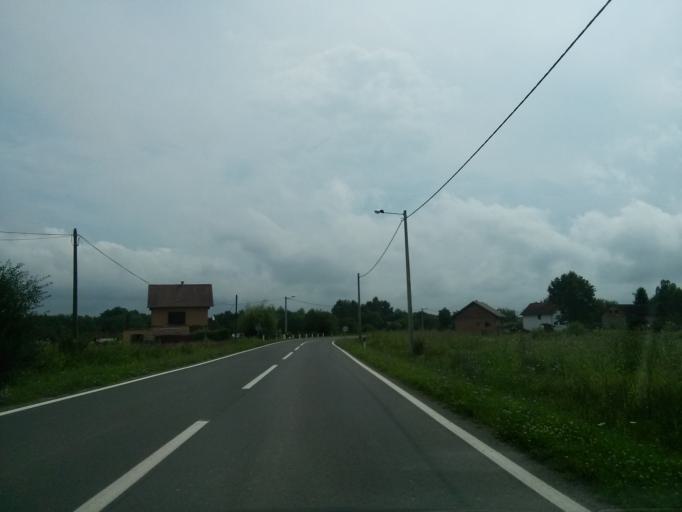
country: HR
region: Sisacko-Moslavacka
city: Glina
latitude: 45.3429
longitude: 16.0501
